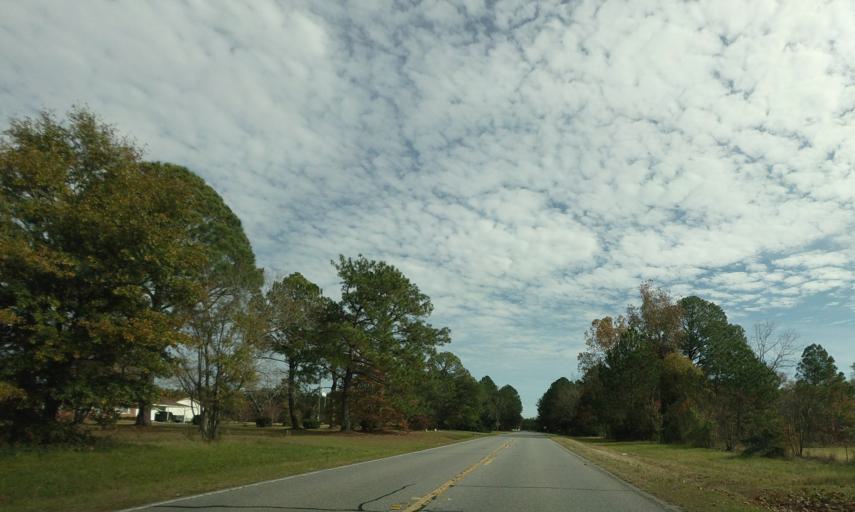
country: US
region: Georgia
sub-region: Bleckley County
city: Cochran
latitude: 32.3949
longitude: -83.2790
